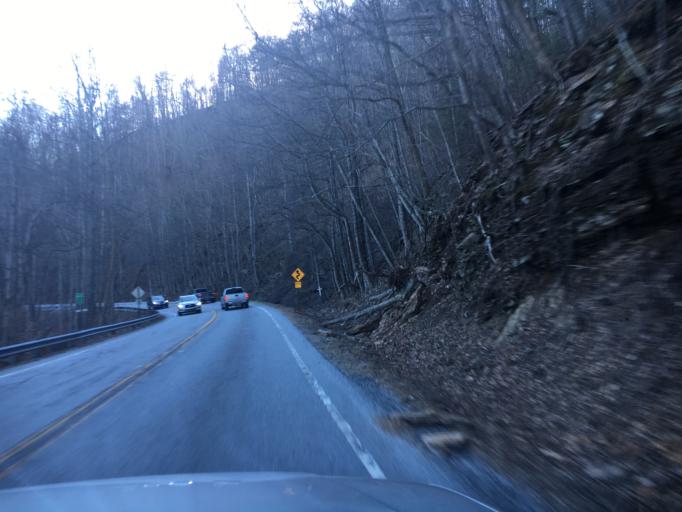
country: US
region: Georgia
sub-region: Union County
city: Blairsville
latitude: 34.7482
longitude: -83.9192
